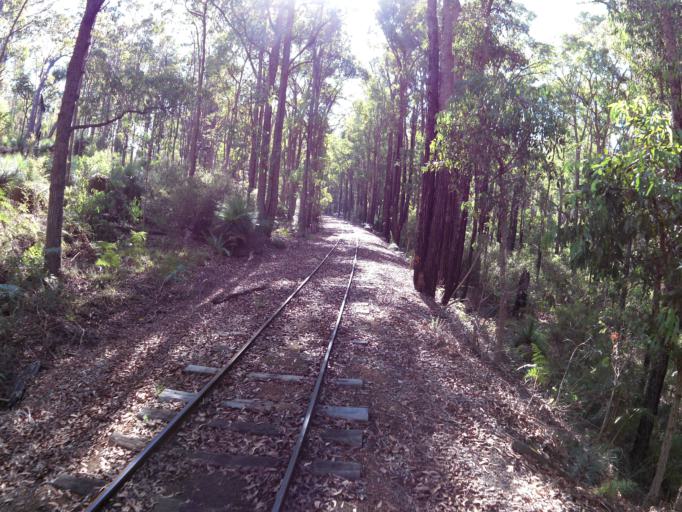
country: AU
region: Western Australia
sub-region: Waroona
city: Waroona
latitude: -32.7234
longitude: 116.1086
